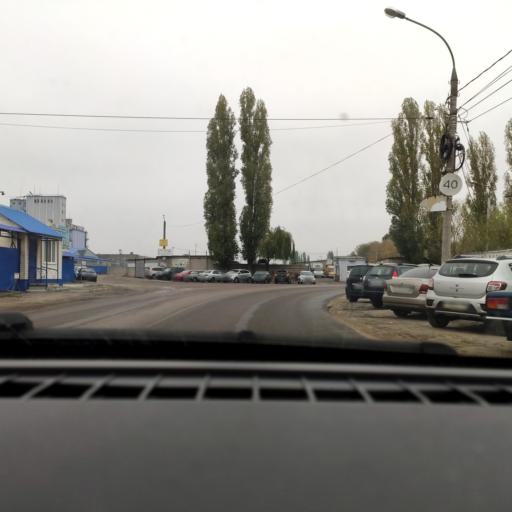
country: RU
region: Voronezj
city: Maslovka
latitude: 51.6364
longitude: 39.2787
